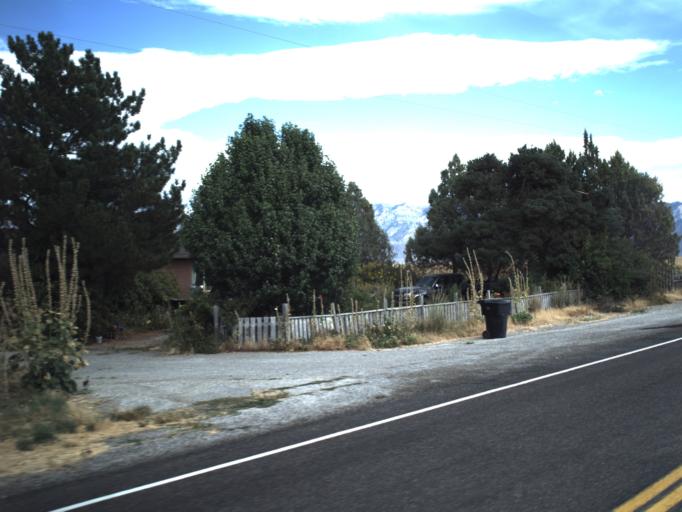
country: US
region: Utah
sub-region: Box Elder County
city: Elwood
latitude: 41.5732
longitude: -112.2172
